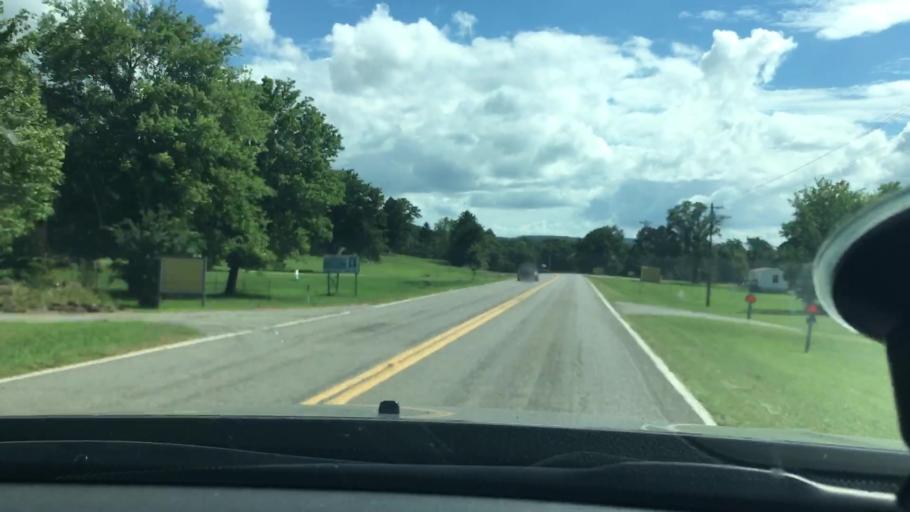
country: US
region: Oklahoma
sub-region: Cherokee County
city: Park Hill
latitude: 35.6965
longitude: -94.9144
